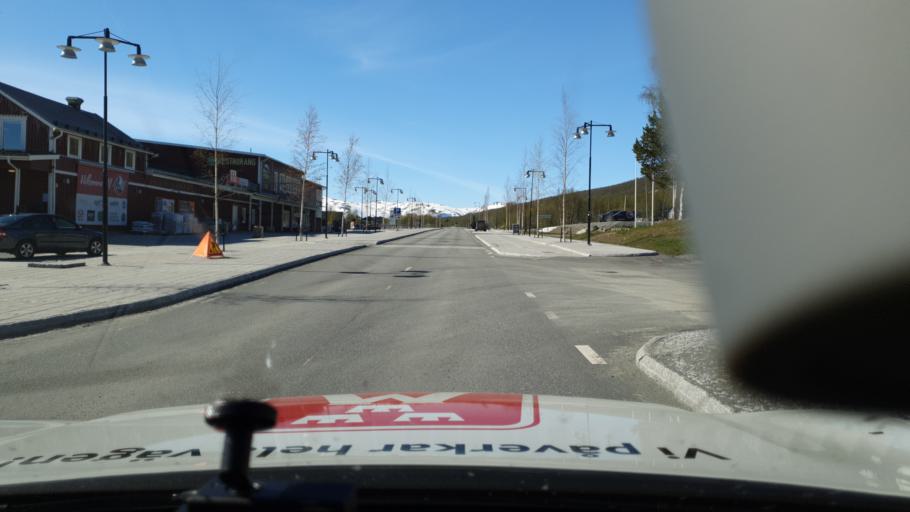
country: NO
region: Nordland
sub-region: Rana
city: Mo i Rana
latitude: 65.8185
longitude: 15.0858
